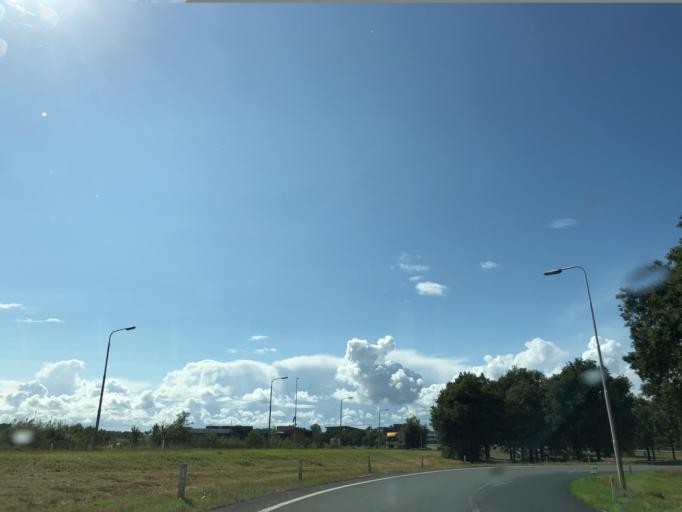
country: NL
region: Friesland
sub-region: Gemeente Smallingerland
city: Drachtstercompagnie
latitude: 53.1032
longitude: 6.1348
